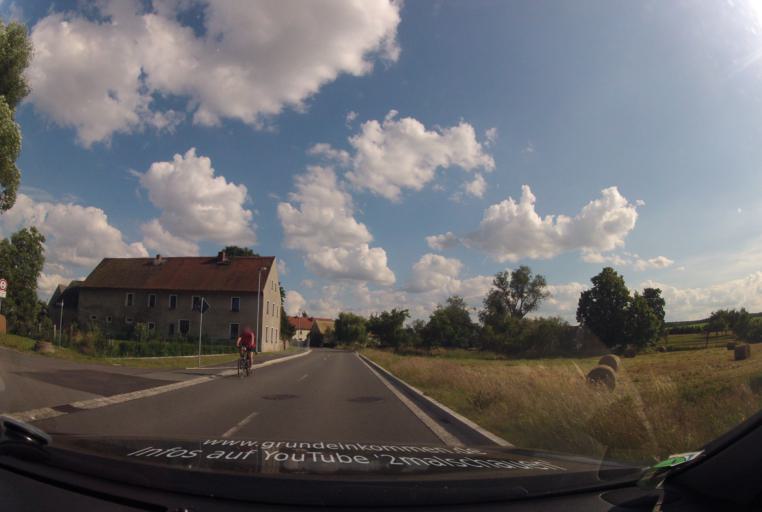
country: DE
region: Saxony
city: Schildau
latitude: 51.4522
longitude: 12.9298
